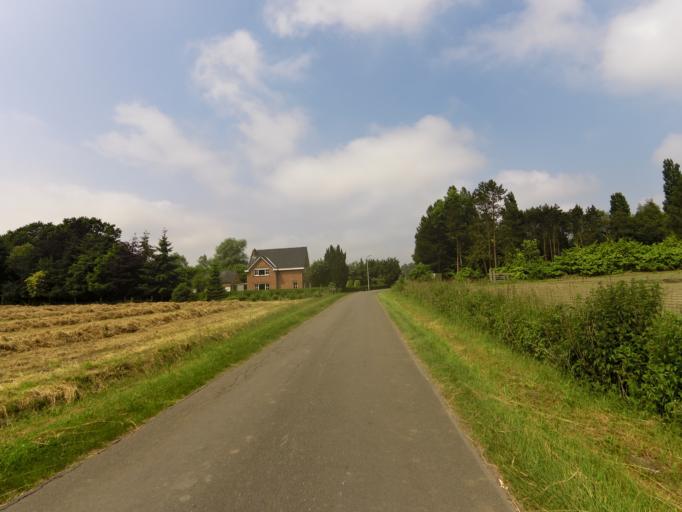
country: BE
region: Flanders
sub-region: Provincie West-Vlaanderen
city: Jabbeke
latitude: 51.1566
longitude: 3.0785
